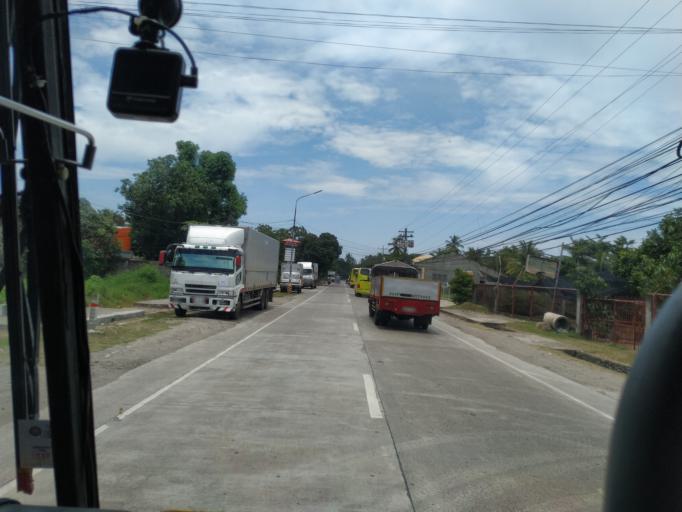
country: PH
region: Central Visayas
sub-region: Province of Negros Oriental
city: Sibulan
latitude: 9.3495
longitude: 123.2859
